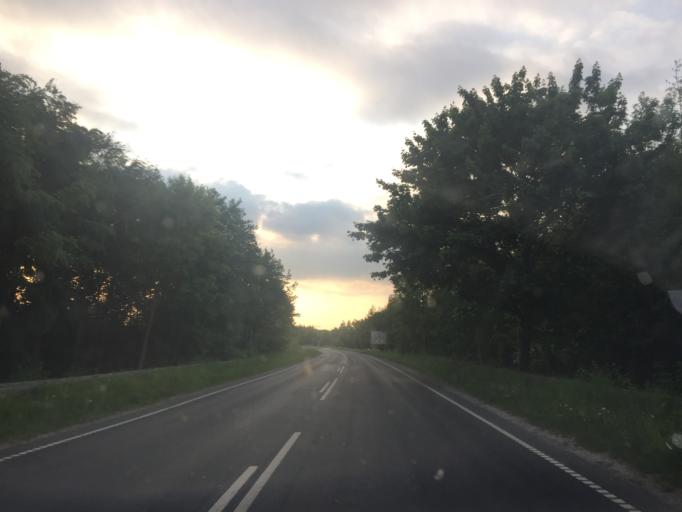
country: DK
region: South Denmark
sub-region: Odense Kommune
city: Neder Holluf
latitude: 55.3570
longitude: 10.4780
